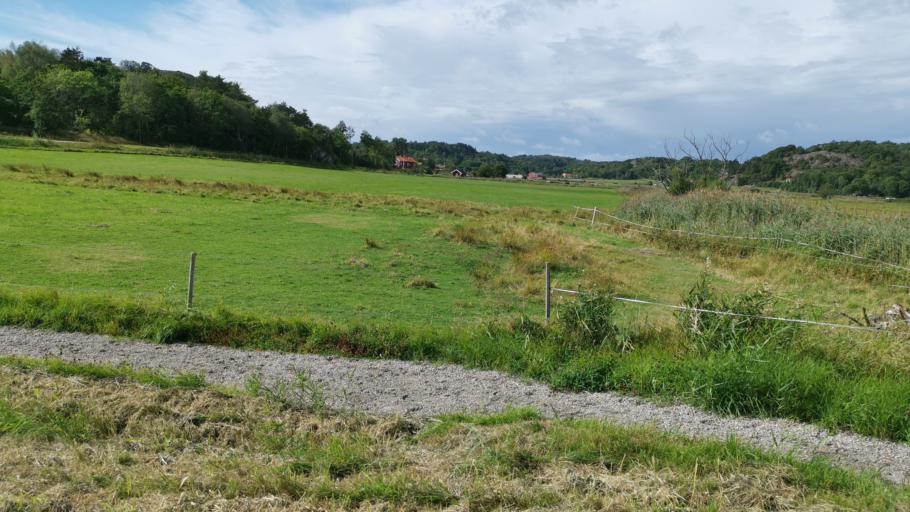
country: SE
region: Vaestra Goetaland
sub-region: Tjorns Kommun
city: Skaerhamn
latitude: 58.0403
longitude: 11.5988
